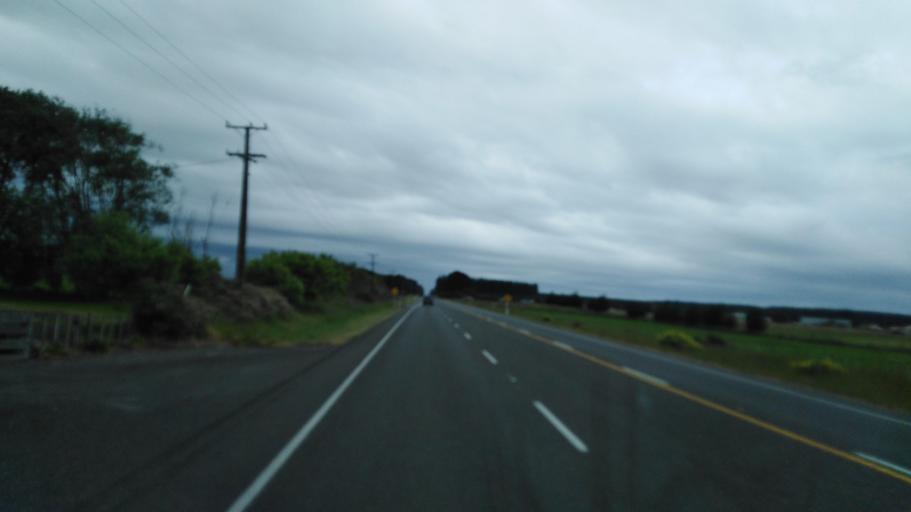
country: NZ
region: Manawatu-Wanganui
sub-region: Horowhenua District
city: Foxton
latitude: -40.4031
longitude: 175.3111
